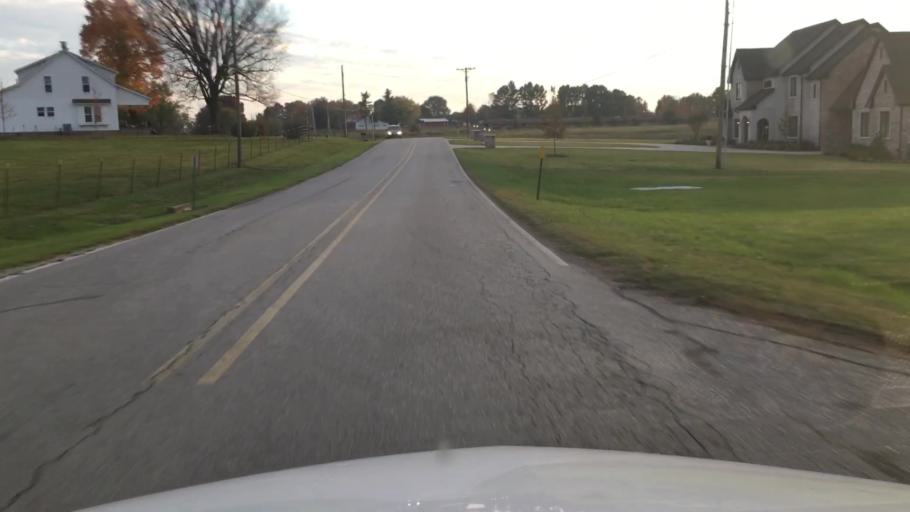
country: US
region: Arkansas
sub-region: Washington County
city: Tontitown
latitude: 36.1835
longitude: -94.2338
